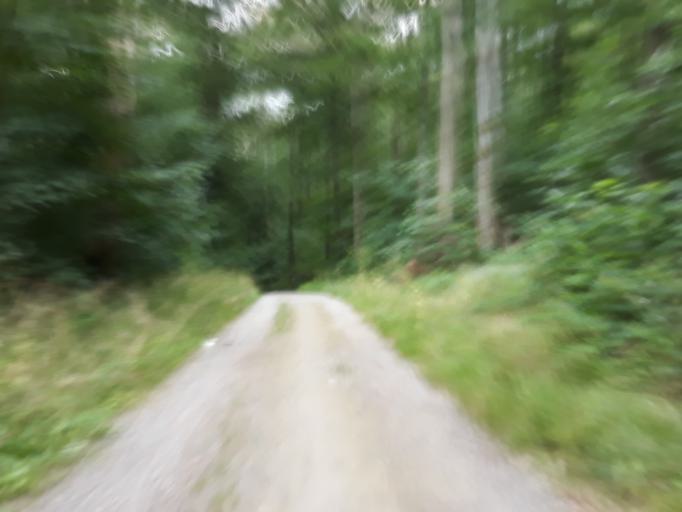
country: DE
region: Baden-Wuerttemberg
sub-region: Regierungsbezirk Stuttgart
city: Schonaich
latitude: 48.6699
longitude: 9.0511
